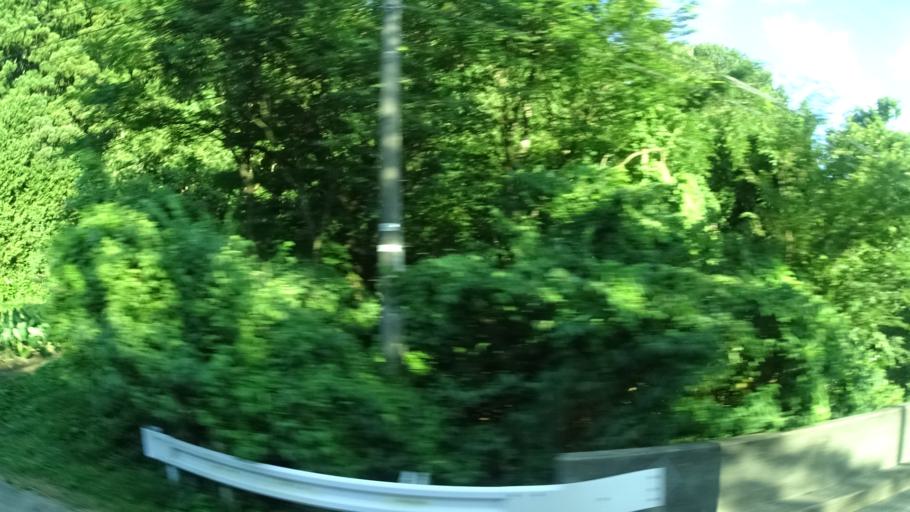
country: JP
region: Ishikawa
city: Nanao
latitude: 37.2956
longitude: 136.8961
